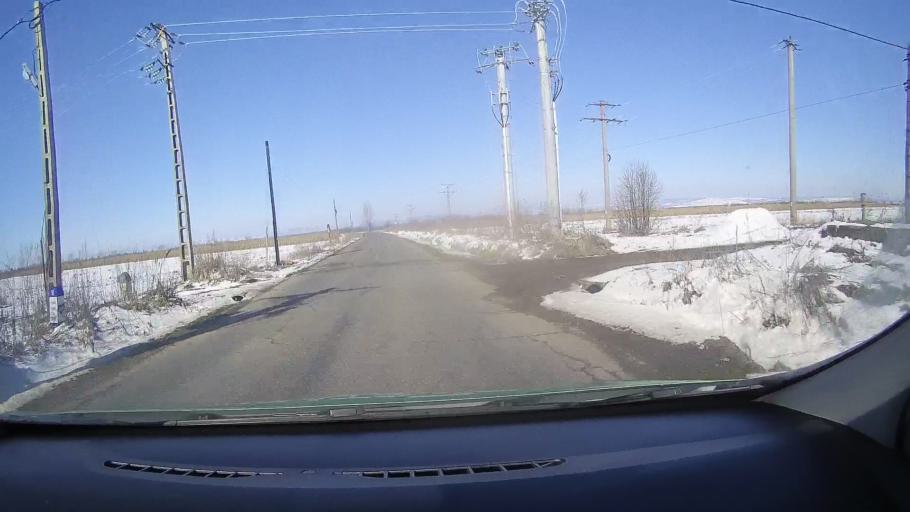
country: RO
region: Brasov
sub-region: Comuna Harseni
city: Harseni
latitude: 45.7635
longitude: 25.0064
